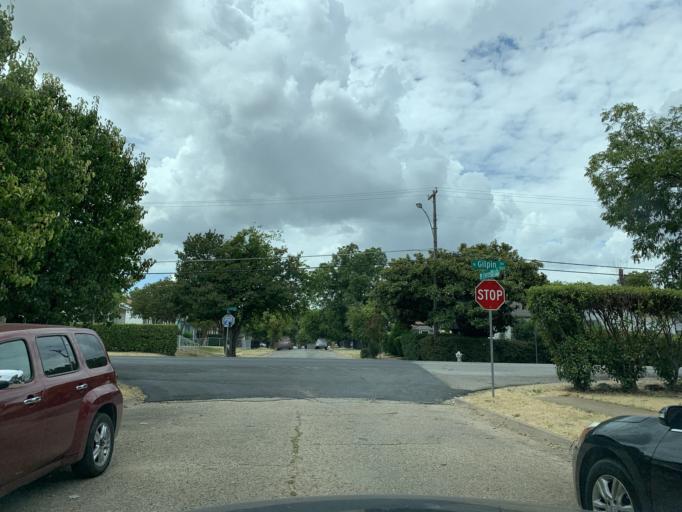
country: US
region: Texas
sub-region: Dallas County
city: Cockrell Hill
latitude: 32.7464
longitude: -96.8804
